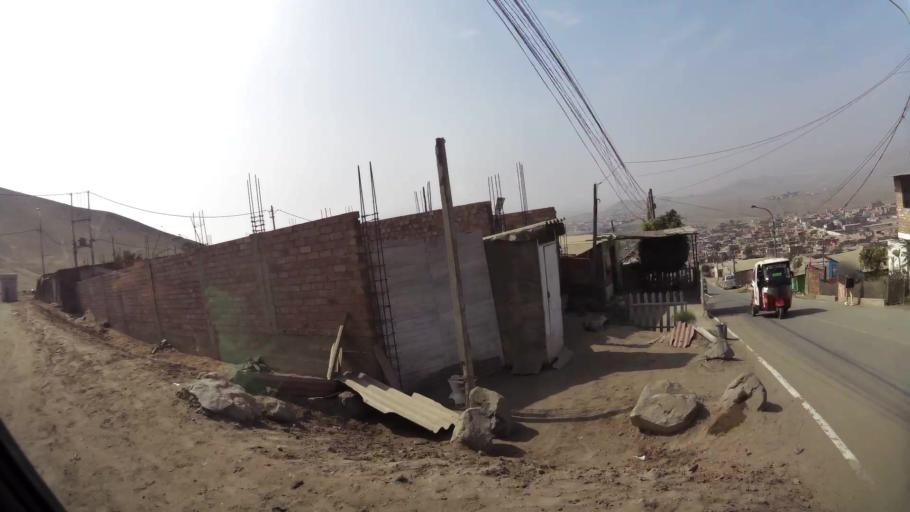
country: PE
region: Lima
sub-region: Lima
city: Santa Rosa
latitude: -11.7855
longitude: -77.1644
